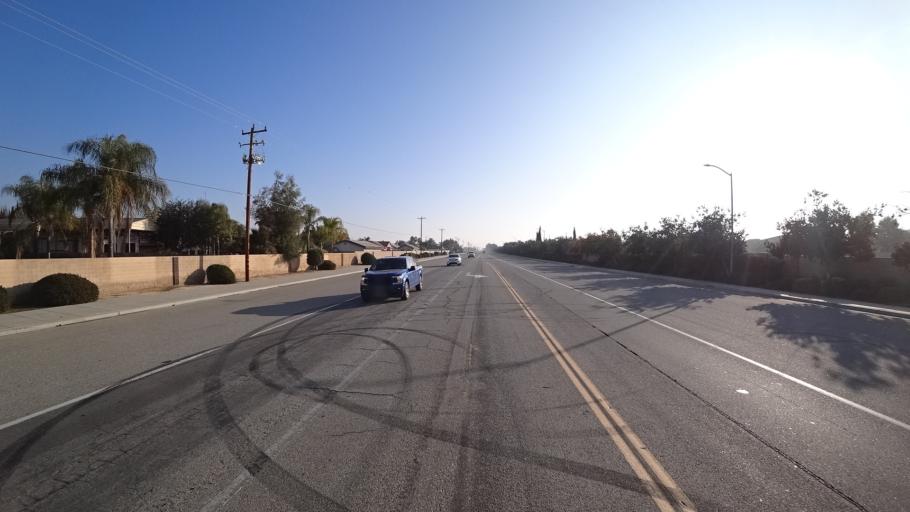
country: US
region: California
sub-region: Kern County
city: Rosedale
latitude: 35.3835
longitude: -119.1714
